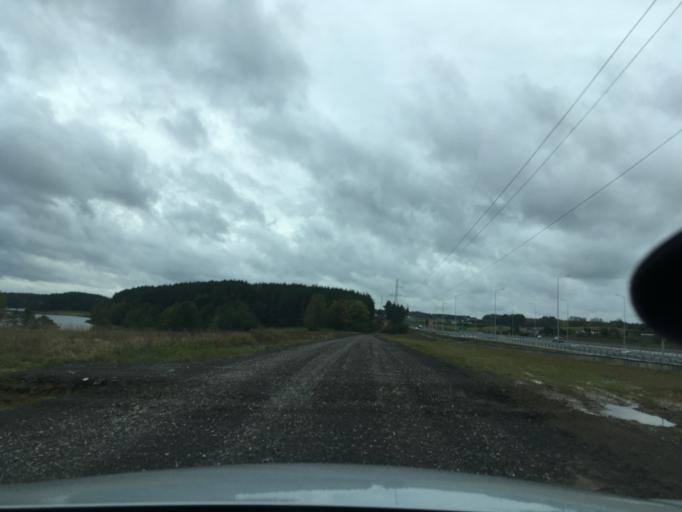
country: PL
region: Pomeranian Voivodeship
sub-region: Powiat koscierski
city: Koscierzyna
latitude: 54.1107
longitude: 17.9970
